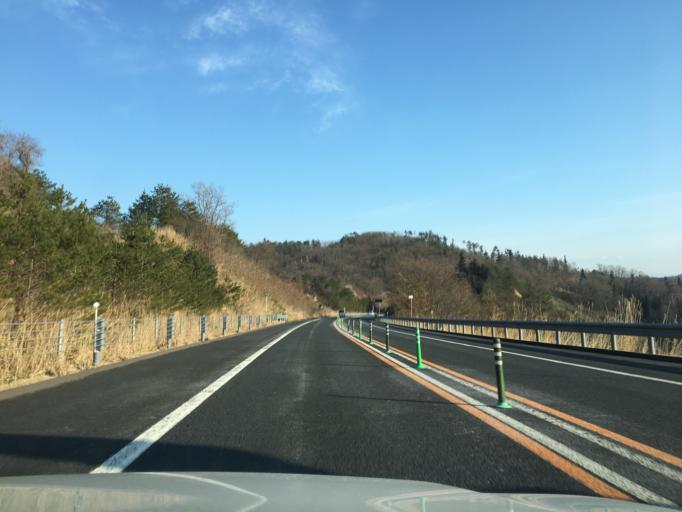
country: JP
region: Yamagata
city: Sagae
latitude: 38.3898
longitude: 140.2180
